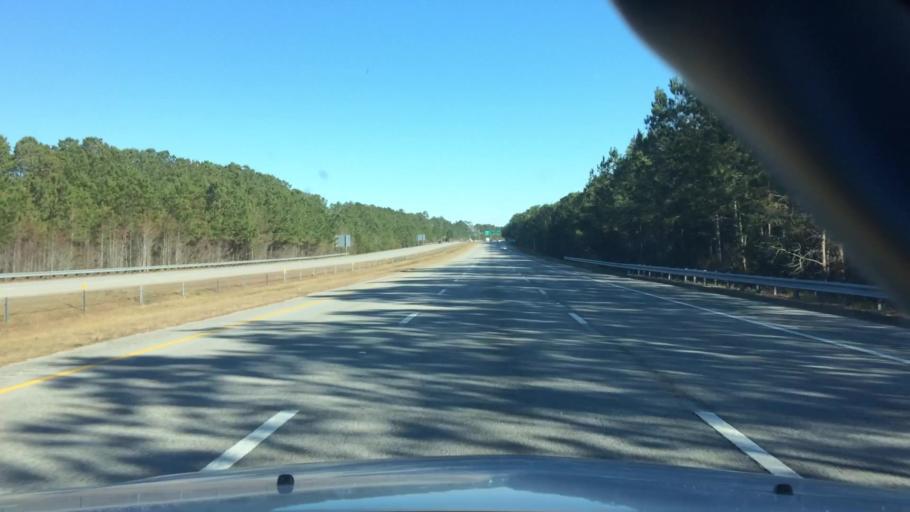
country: US
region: South Carolina
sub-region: Horry County
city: North Myrtle Beach
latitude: 33.8548
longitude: -78.6972
